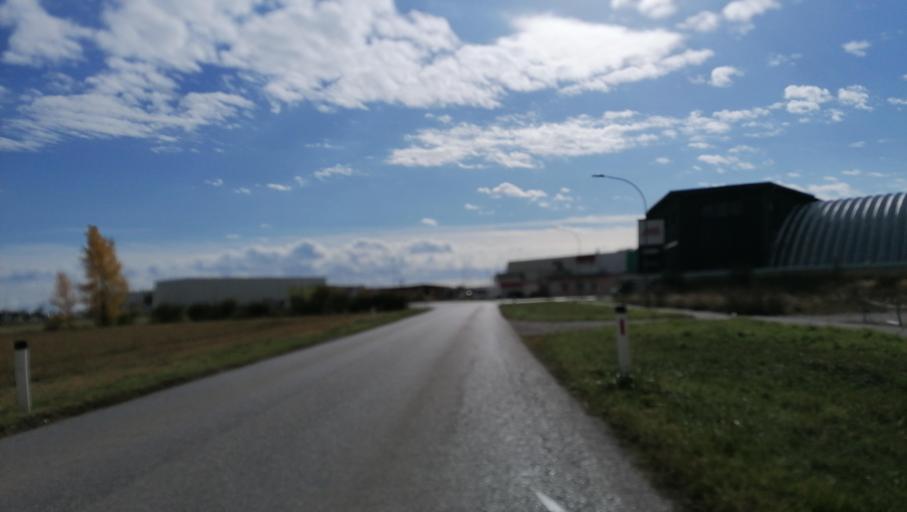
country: AT
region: Lower Austria
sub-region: Politischer Bezirk Baden
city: Teesdorf
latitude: 47.9762
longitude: 16.2784
